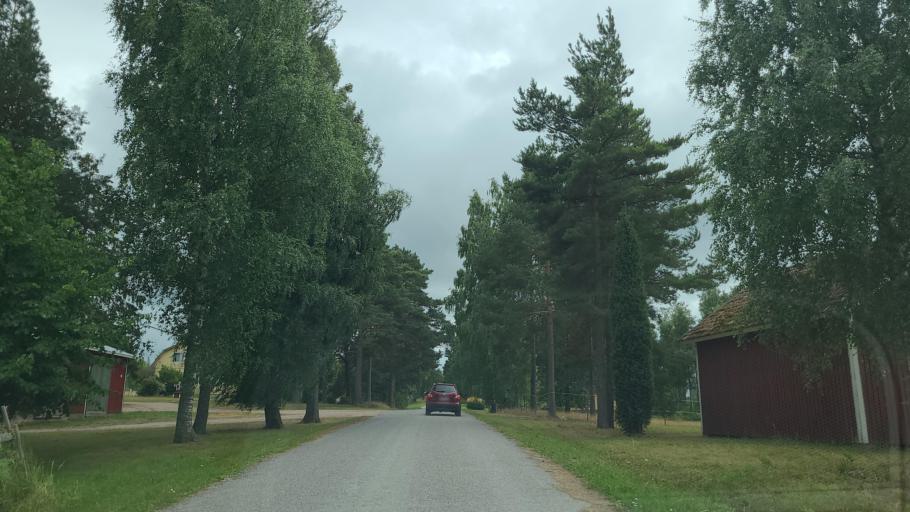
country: FI
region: Varsinais-Suomi
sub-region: Aboland-Turunmaa
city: Dragsfjaerd
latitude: 60.0848
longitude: 22.4150
